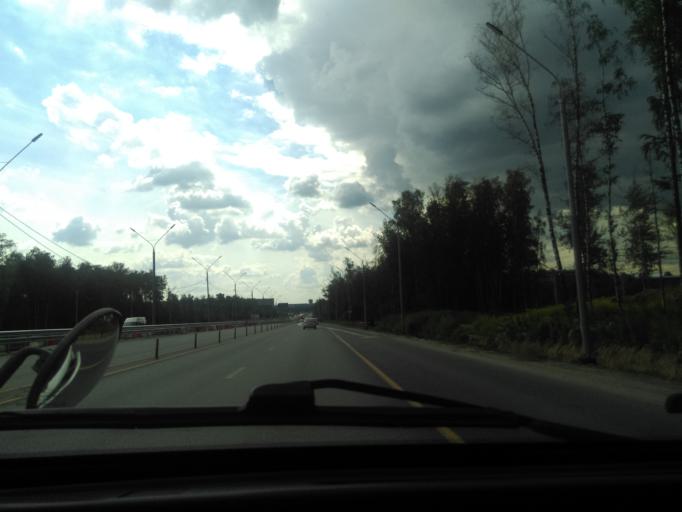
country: RU
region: Moskovskaya
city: Yakovlevskoye
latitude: 55.4266
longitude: 37.8850
